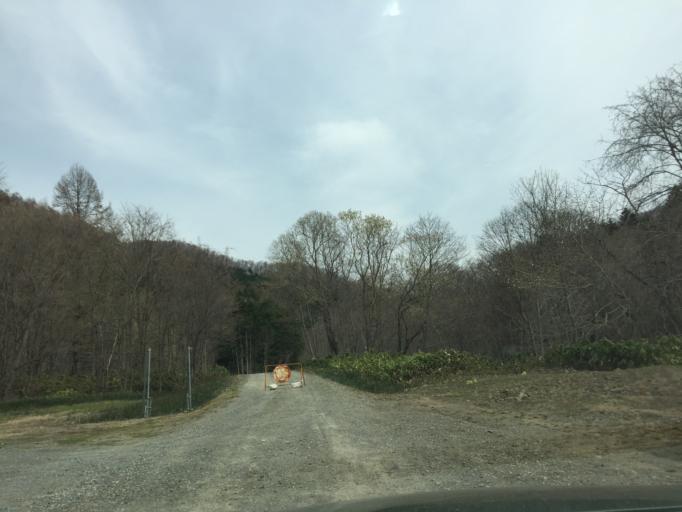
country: JP
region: Hokkaido
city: Ashibetsu
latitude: 43.6239
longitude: 142.2276
